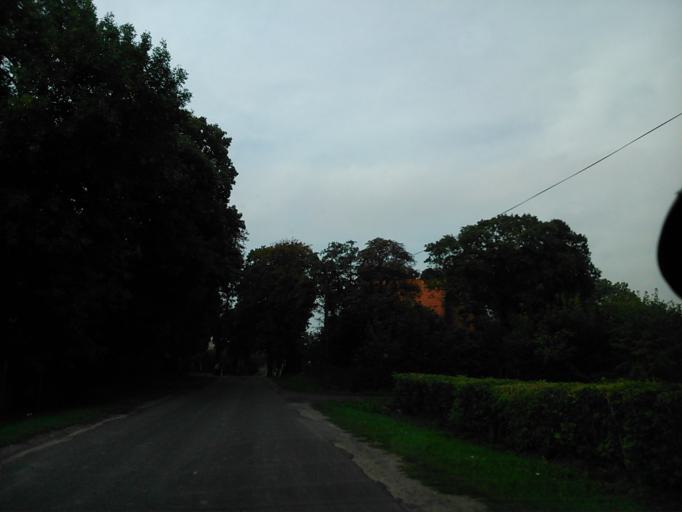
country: PL
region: Kujawsko-Pomorskie
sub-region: Powiat golubsko-dobrzynski
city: Kowalewo Pomorskie
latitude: 53.1969
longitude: 18.8218
